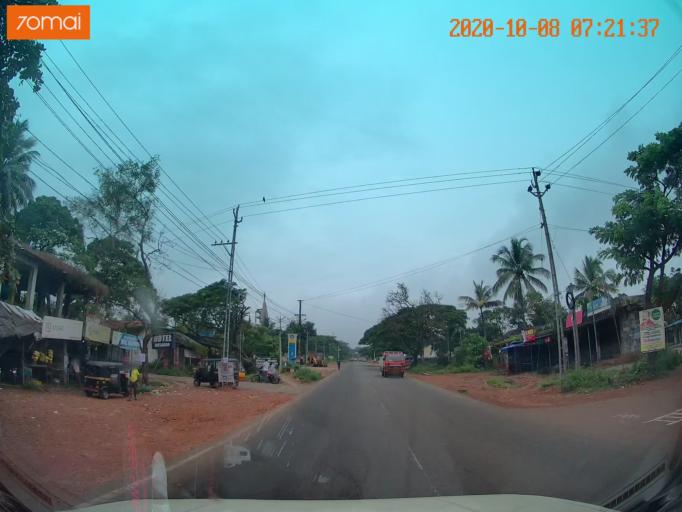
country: IN
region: Kerala
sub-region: Malappuram
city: Tirur
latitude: 10.8570
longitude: 76.0368
